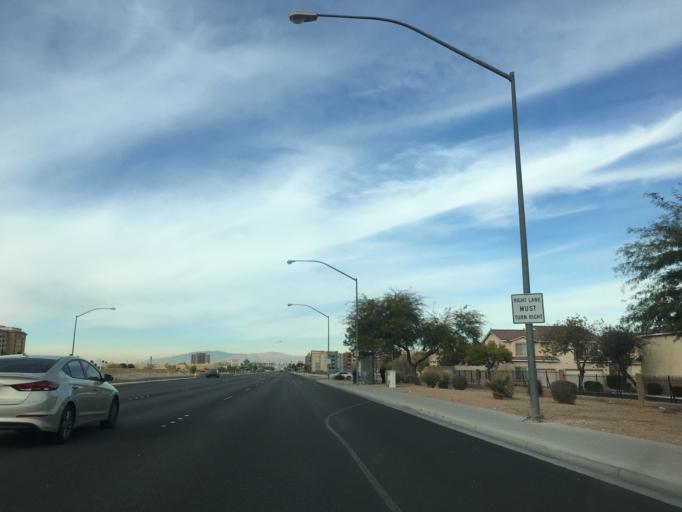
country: US
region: Nevada
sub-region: Clark County
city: Enterprise
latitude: 36.0164
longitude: -115.1723
